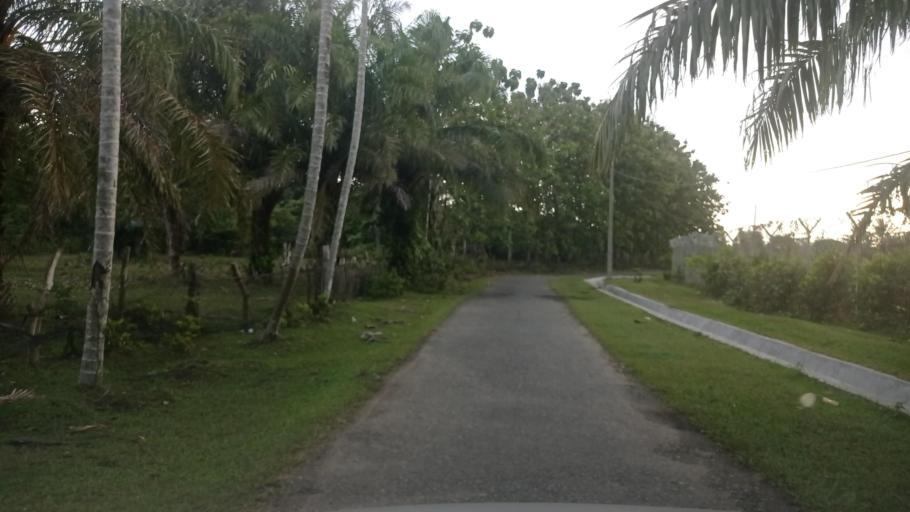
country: ID
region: Jambi
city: Sungai Penuh
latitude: -2.5478
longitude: 101.0886
